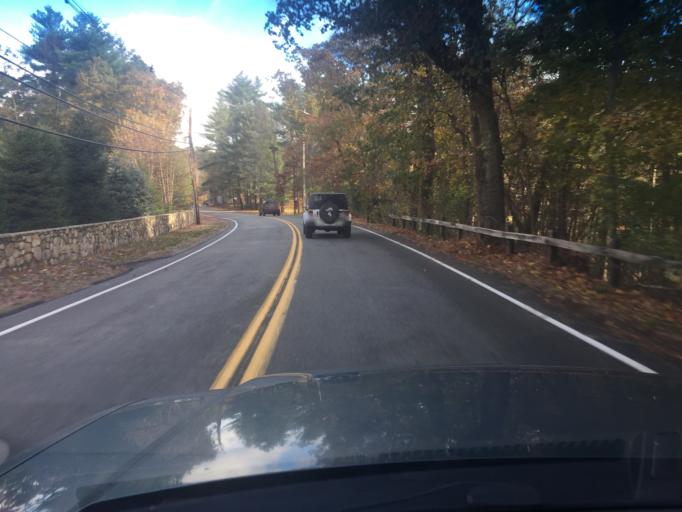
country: US
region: Massachusetts
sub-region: Norfolk County
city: Dover
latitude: 42.2333
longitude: -71.2866
